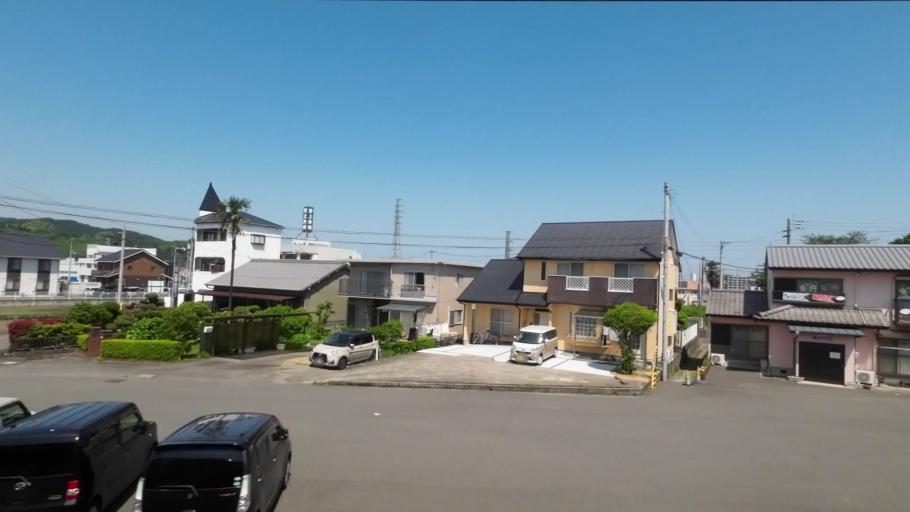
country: JP
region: Ehime
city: Niihama
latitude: 33.9444
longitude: 133.2906
